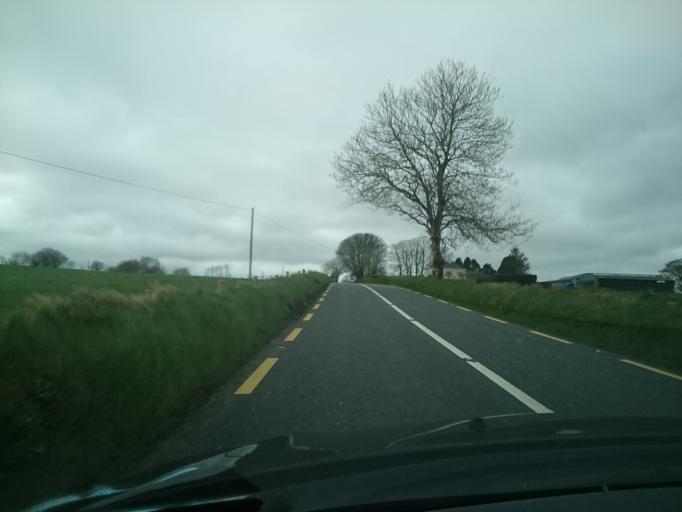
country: IE
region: Connaught
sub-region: Maigh Eo
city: Ballyhaunis
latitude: 53.7458
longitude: -8.8042
